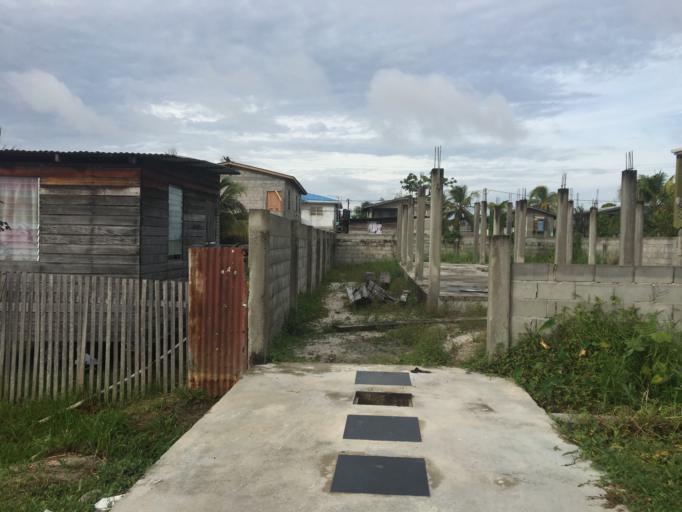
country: GY
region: Demerara-Mahaica
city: Georgetown
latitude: 6.8030
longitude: -58.1246
